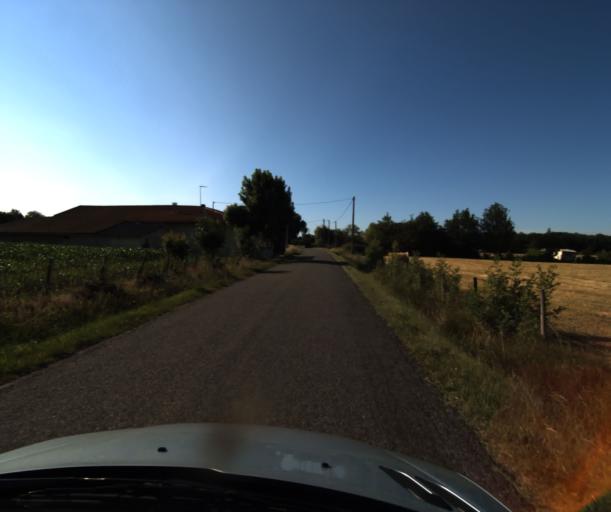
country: FR
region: Midi-Pyrenees
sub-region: Departement du Tarn-et-Garonne
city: Saint-Porquier
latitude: 44.0571
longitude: 1.2091
